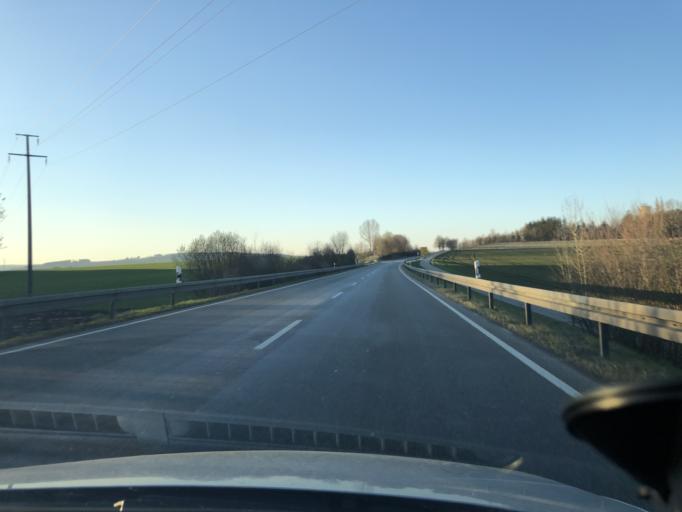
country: DE
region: Baden-Wuerttemberg
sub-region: Freiburg Region
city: Hufingen
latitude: 47.9109
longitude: 8.5057
